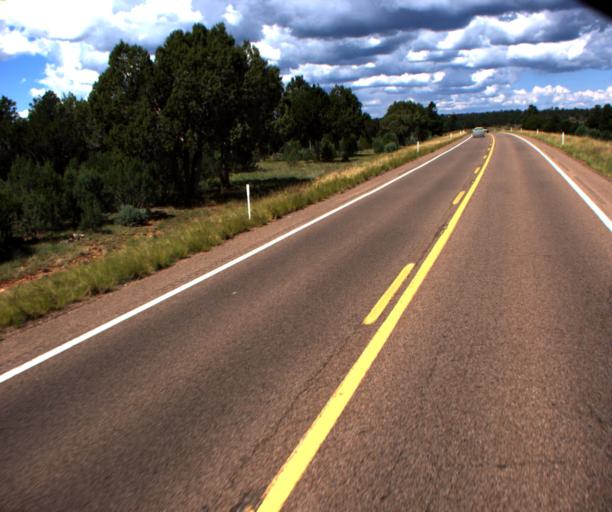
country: US
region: Arizona
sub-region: Navajo County
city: Heber-Overgaard
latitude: 34.3913
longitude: -110.5084
